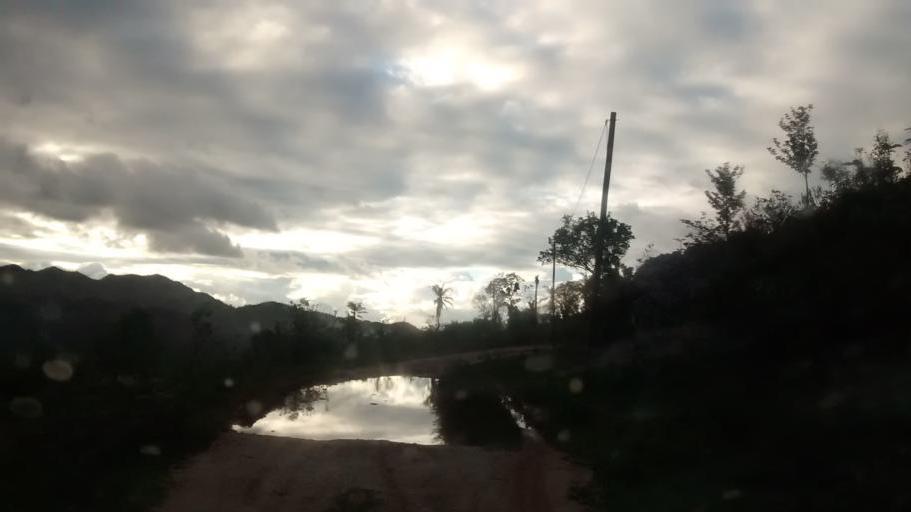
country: HT
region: Grandans
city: Corail
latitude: 18.4775
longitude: -73.7992
